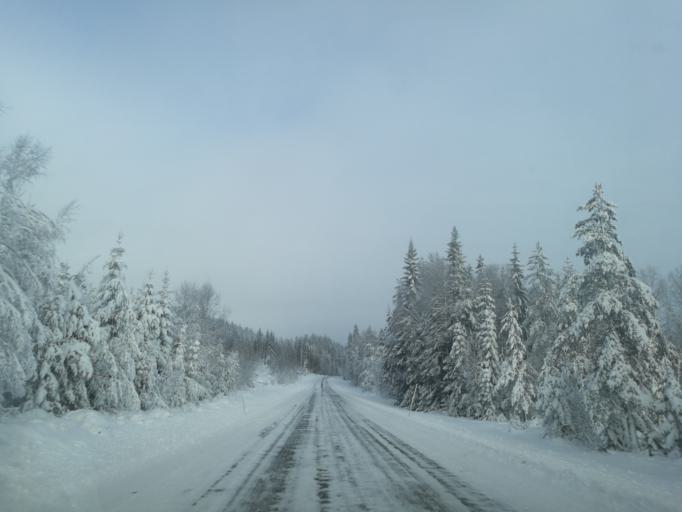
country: SE
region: Vaermland
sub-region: Torsby Kommun
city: Torsby
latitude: 60.5941
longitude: 12.7329
